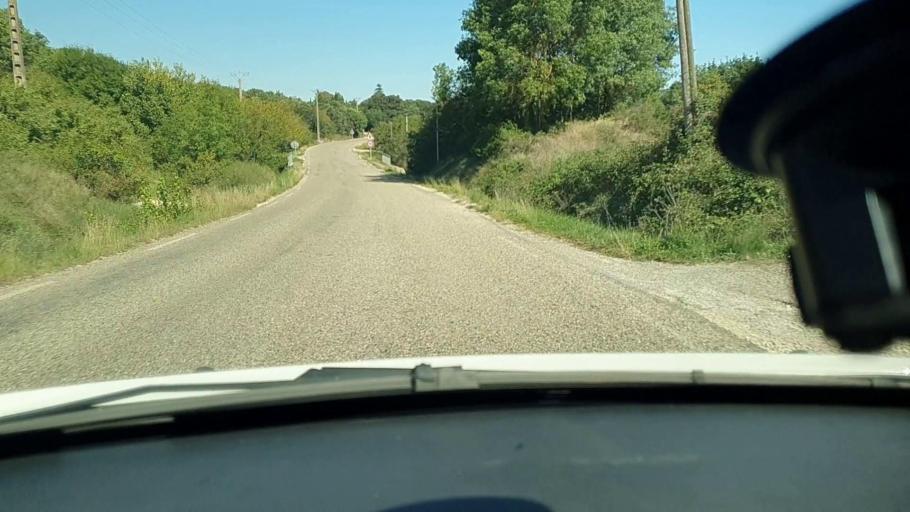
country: FR
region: Languedoc-Roussillon
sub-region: Departement du Gard
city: Goudargues
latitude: 44.1520
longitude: 4.4540
